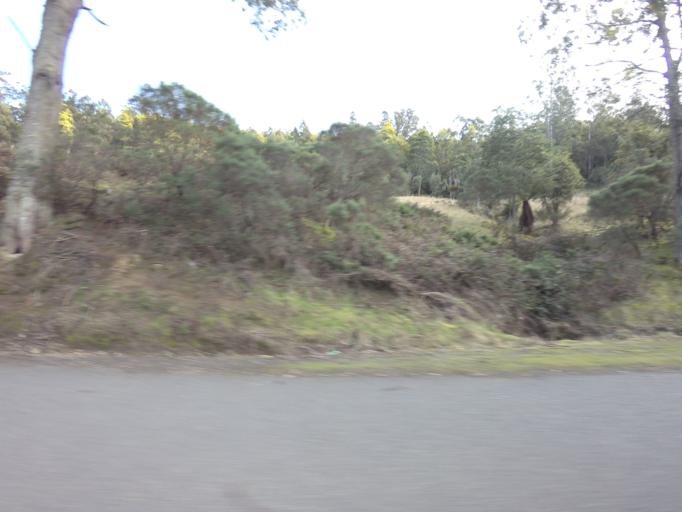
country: AU
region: Tasmania
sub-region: Kingborough
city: Margate
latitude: -43.0227
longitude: 147.1612
